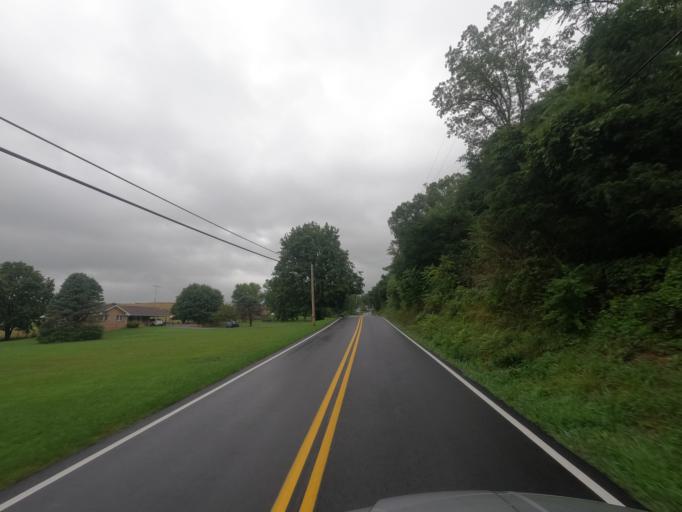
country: US
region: Maryland
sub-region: Washington County
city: Wilson-Conococheague
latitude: 39.6396
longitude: -77.9333
